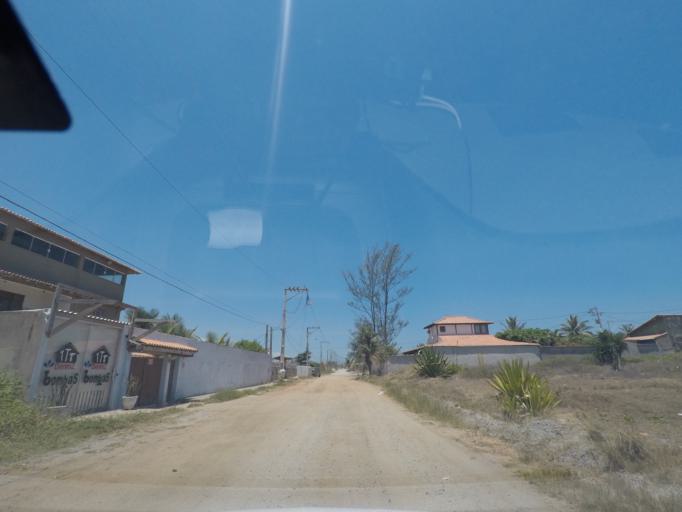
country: BR
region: Rio de Janeiro
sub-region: Marica
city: Marica
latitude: -22.9688
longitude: -42.9655
